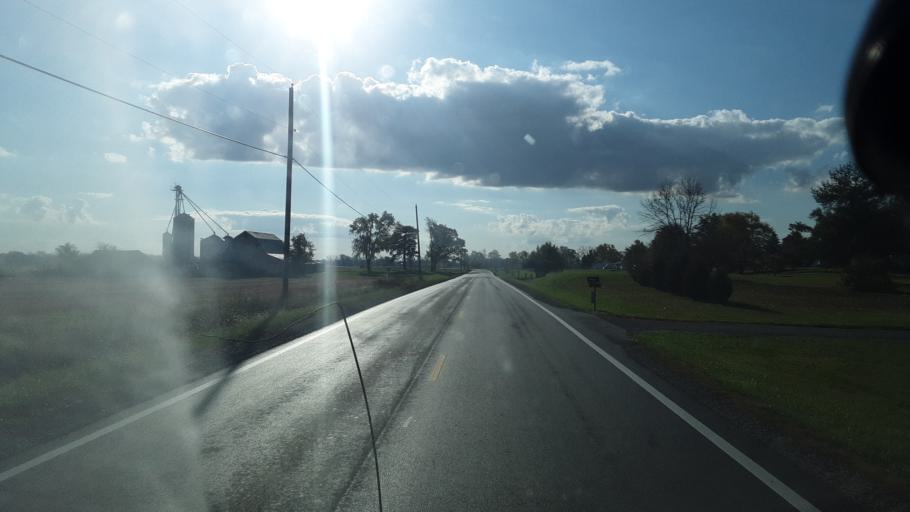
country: US
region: Ohio
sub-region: Fayette County
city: Jeffersonville
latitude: 39.5929
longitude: -83.5109
